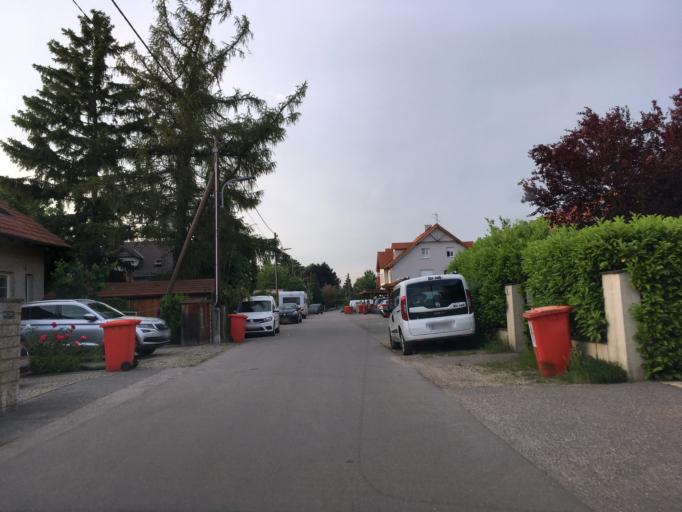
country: AT
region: Lower Austria
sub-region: Politischer Bezirk Wien-Umgebung
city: Gerasdorf bei Wien
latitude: 48.3138
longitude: 16.5018
